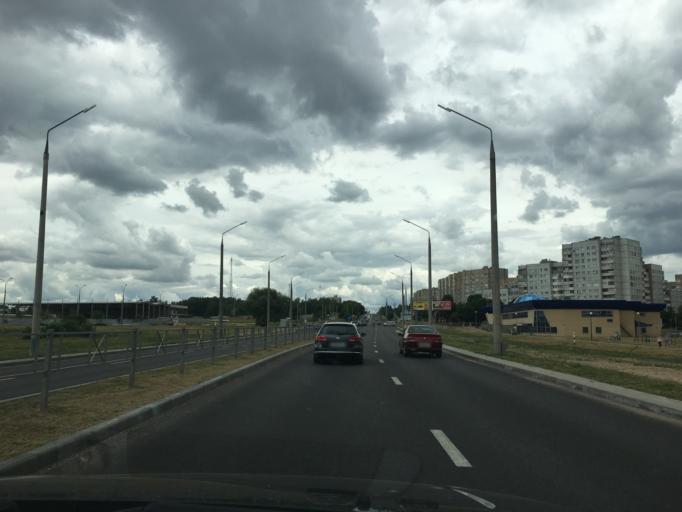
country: BY
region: Grodnenskaya
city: Hrodna
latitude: 53.6395
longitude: 23.8458
